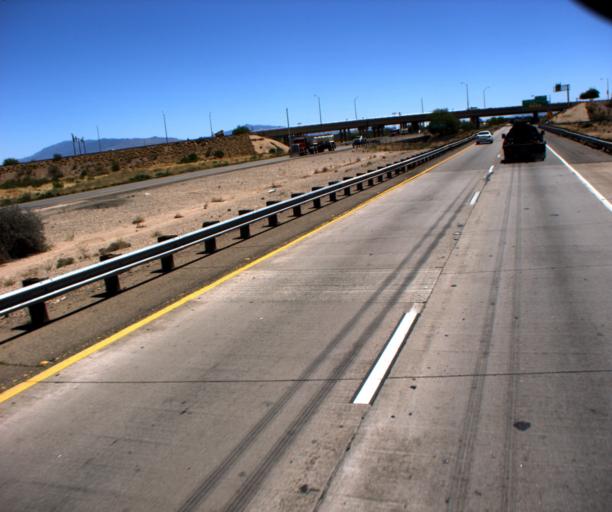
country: US
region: Arizona
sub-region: Pima County
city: South Tucson
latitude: 32.1785
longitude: -110.9471
